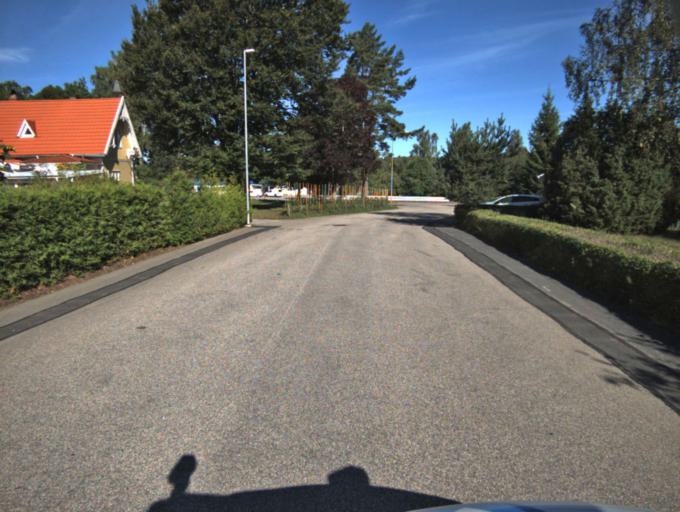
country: SE
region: Vaestra Goetaland
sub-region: Ulricehamns Kommun
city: Ulricehamn
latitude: 57.8972
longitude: 13.4629
